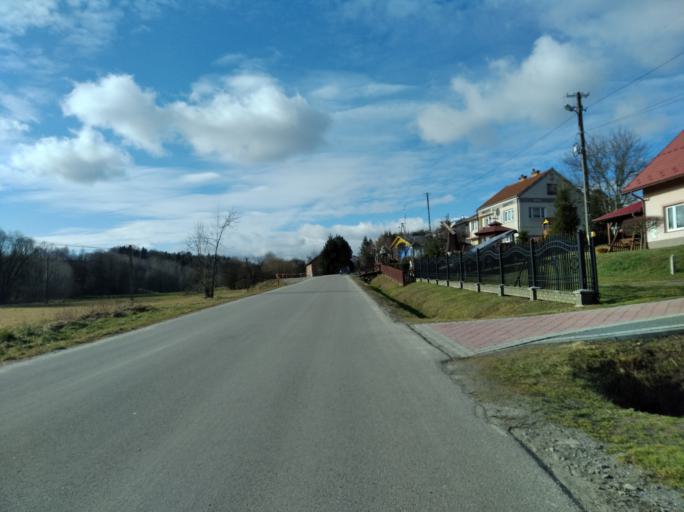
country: PL
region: Subcarpathian Voivodeship
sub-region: Powiat strzyzowski
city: Wisniowa
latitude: 49.9132
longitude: 21.6743
